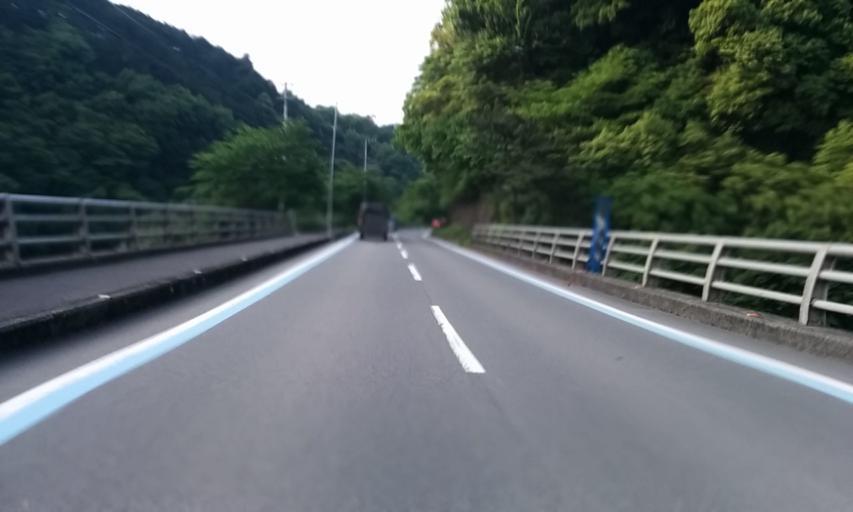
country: JP
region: Ehime
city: Saijo
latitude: 33.8754
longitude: 133.1739
